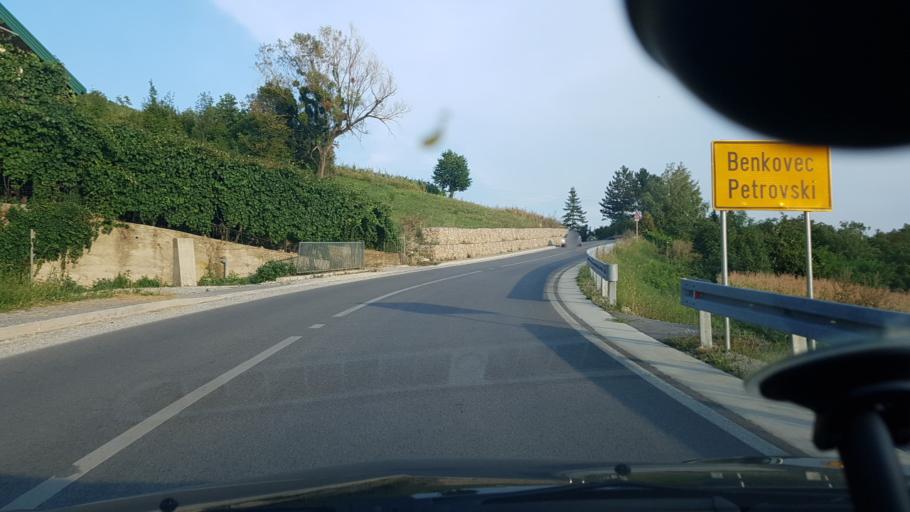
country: HR
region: Krapinsko-Zagorska
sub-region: Grad Krapina
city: Krapina
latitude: 46.1722
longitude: 15.8318
